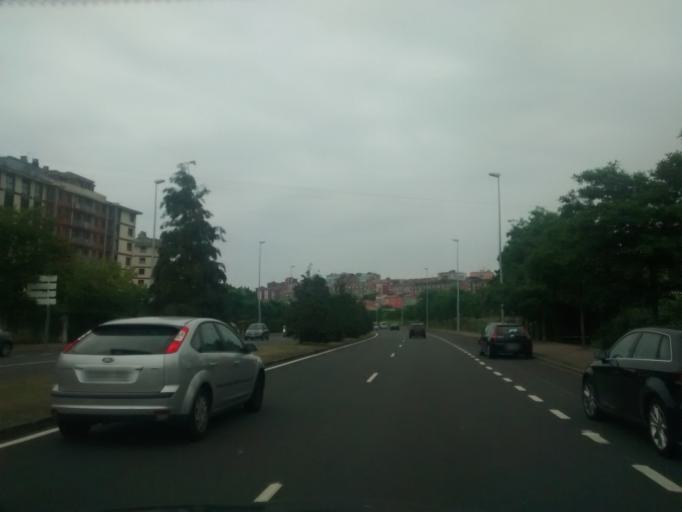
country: ES
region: Cantabria
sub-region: Provincia de Cantabria
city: Santander
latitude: 43.4670
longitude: -3.8303
